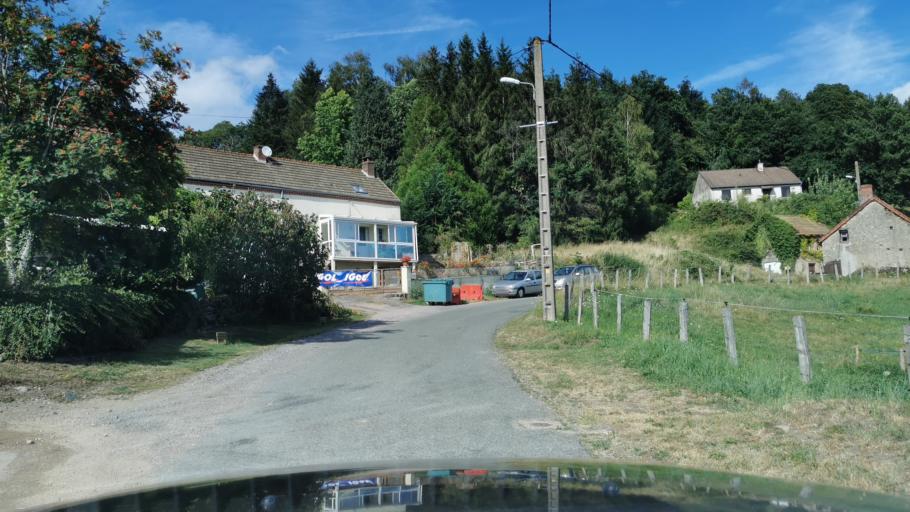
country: FR
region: Bourgogne
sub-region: Departement de Saone-et-Loire
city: Marmagne
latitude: 46.8741
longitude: 4.3385
